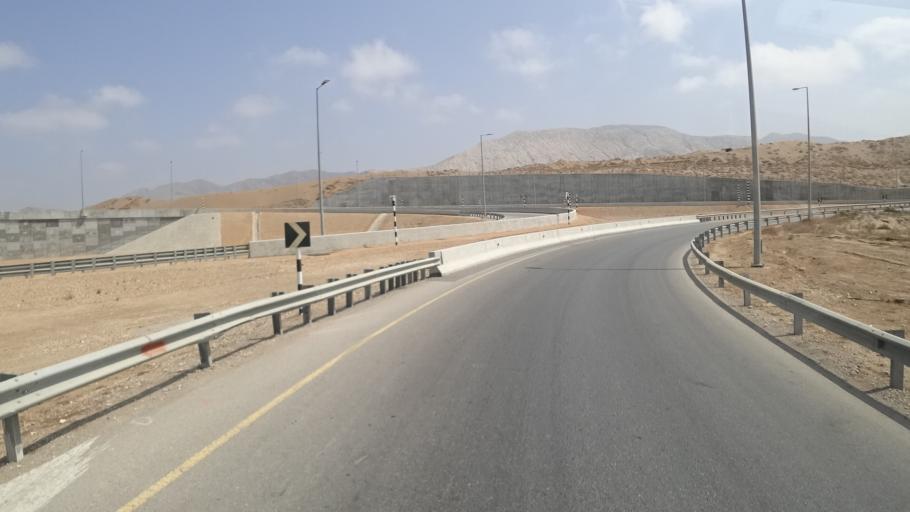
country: OM
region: Muhafazat Masqat
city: Bawshar
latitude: 23.5691
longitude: 58.4086
